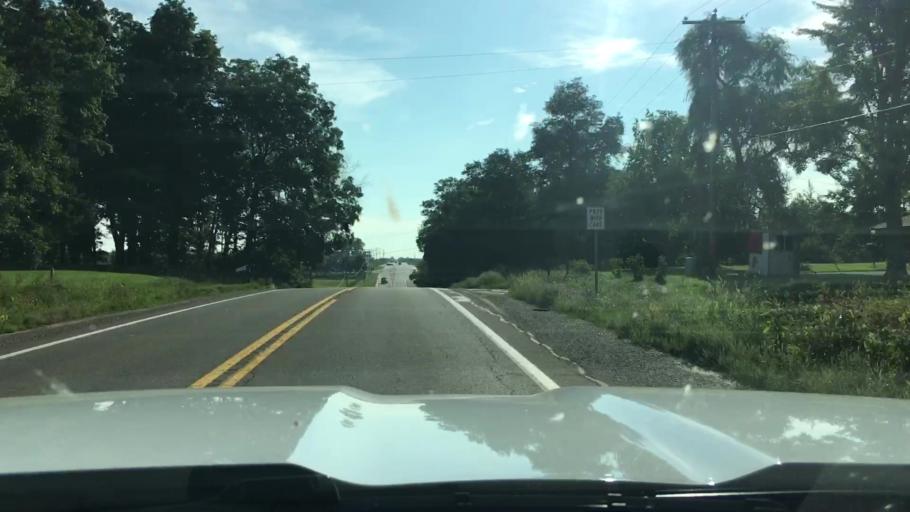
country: US
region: Michigan
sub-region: Kent County
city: Cedar Springs
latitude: 43.2197
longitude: -85.5874
